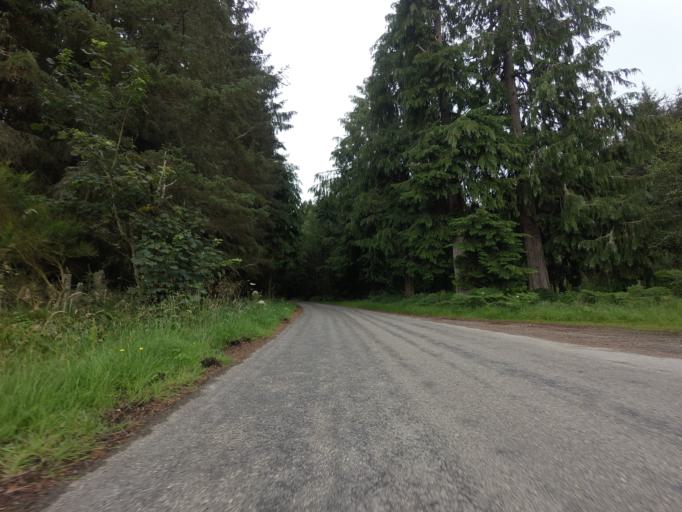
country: GB
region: Scotland
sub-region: Highland
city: Evanton
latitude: 57.8903
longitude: -4.3833
